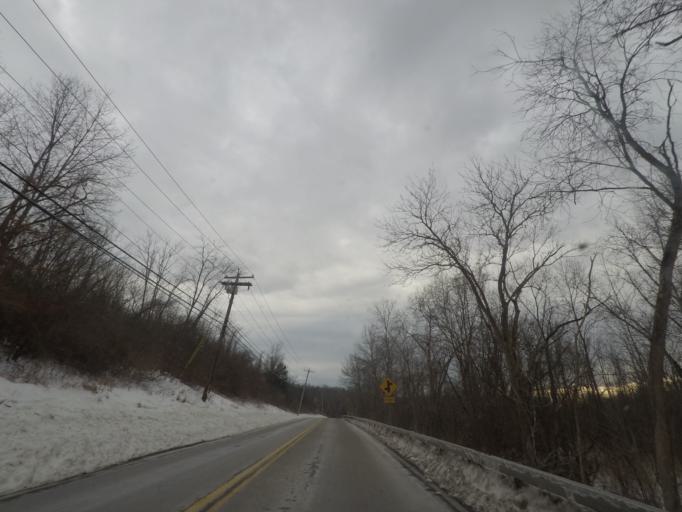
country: US
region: New York
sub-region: Rensselaer County
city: Castleton-on-Hudson
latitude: 42.5235
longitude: -73.7576
